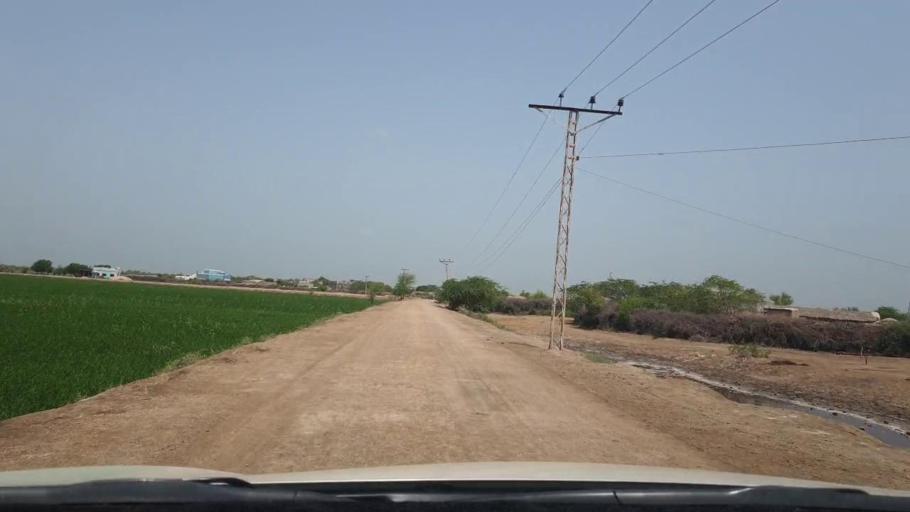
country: PK
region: Sindh
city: Talhar
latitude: 24.9240
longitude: 68.8380
